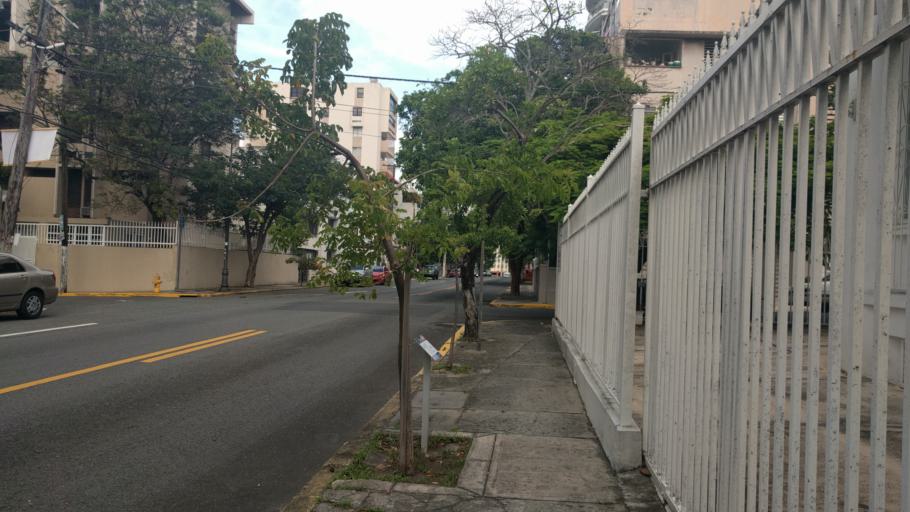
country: PR
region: San Juan
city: San Juan
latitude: 18.4527
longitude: -66.0845
